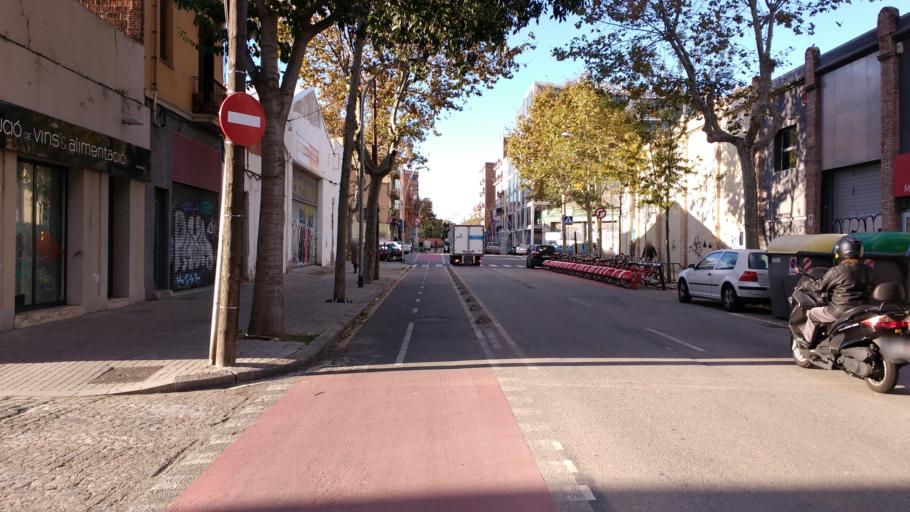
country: ES
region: Catalonia
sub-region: Provincia de Barcelona
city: Sant Marti
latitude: 41.3964
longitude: 2.1939
